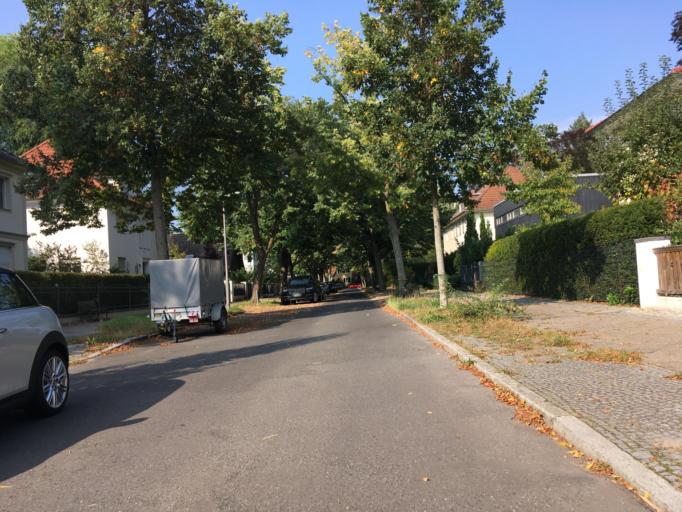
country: DE
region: Berlin
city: Zehlendorf Bezirk
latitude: 52.4354
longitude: 13.2434
